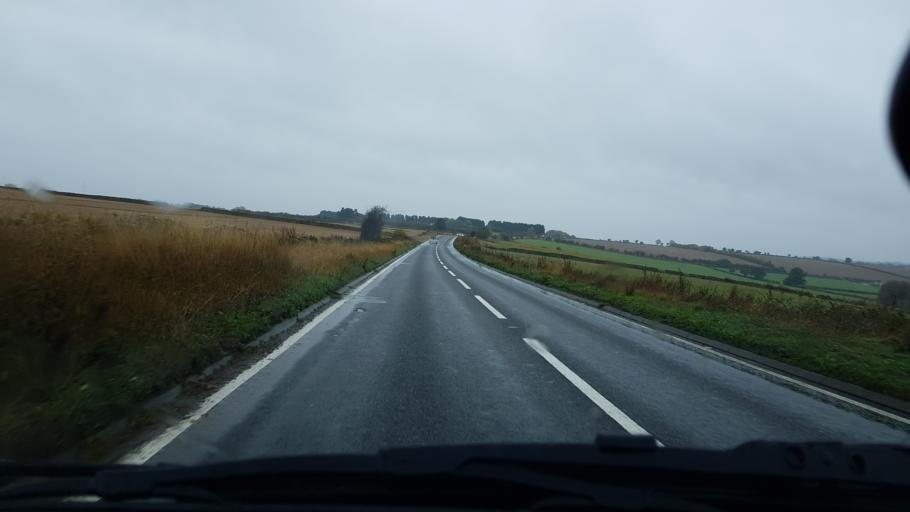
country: GB
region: England
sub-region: Oxfordshire
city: Carterton
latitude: 51.7899
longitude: -1.5869
